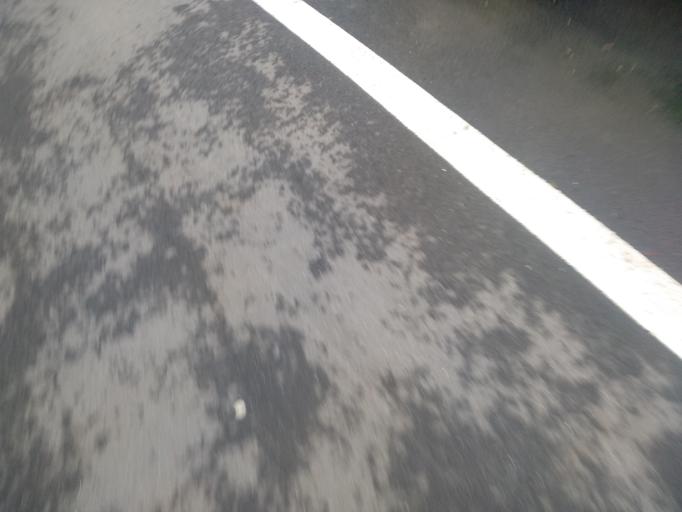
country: TW
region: Taiwan
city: Taoyuan City
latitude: 24.9980
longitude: 121.1616
